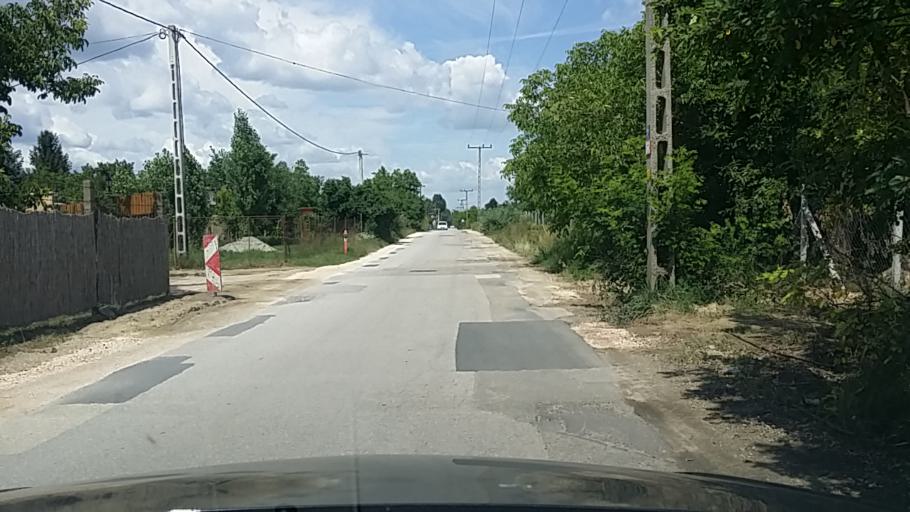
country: HU
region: Bacs-Kiskun
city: Kecskemet
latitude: 46.9227
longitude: 19.6564
